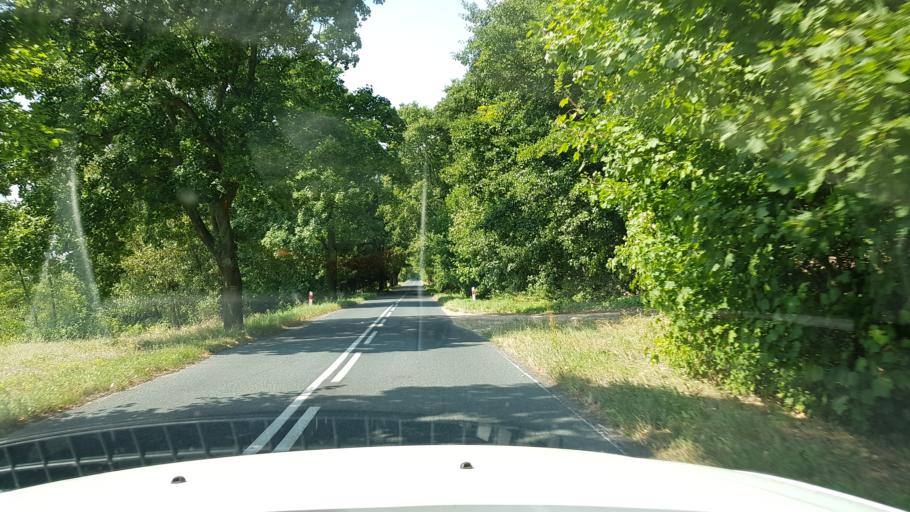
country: PL
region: West Pomeranian Voivodeship
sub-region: Powiat gryfinski
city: Cedynia
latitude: 52.8320
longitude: 14.2103
